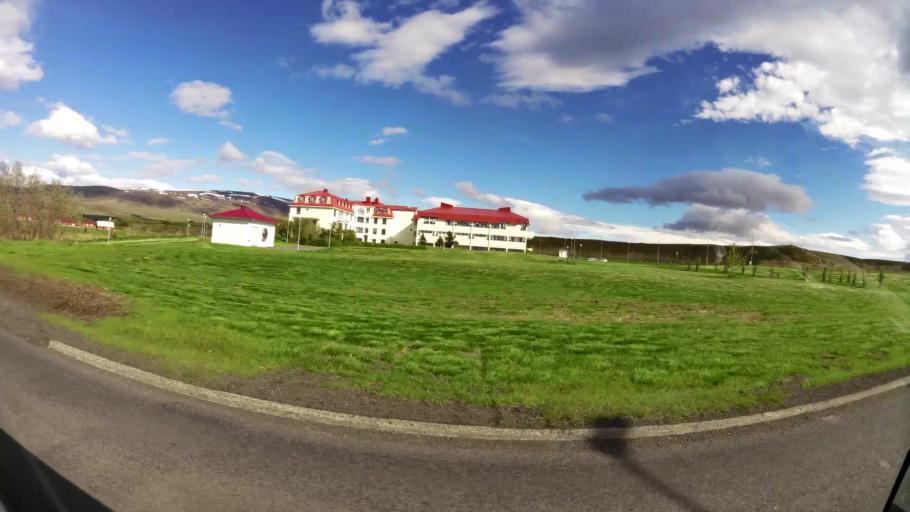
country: IS
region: Northwest
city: Saudarkrokur
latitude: 65.6569
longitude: -20.2831
